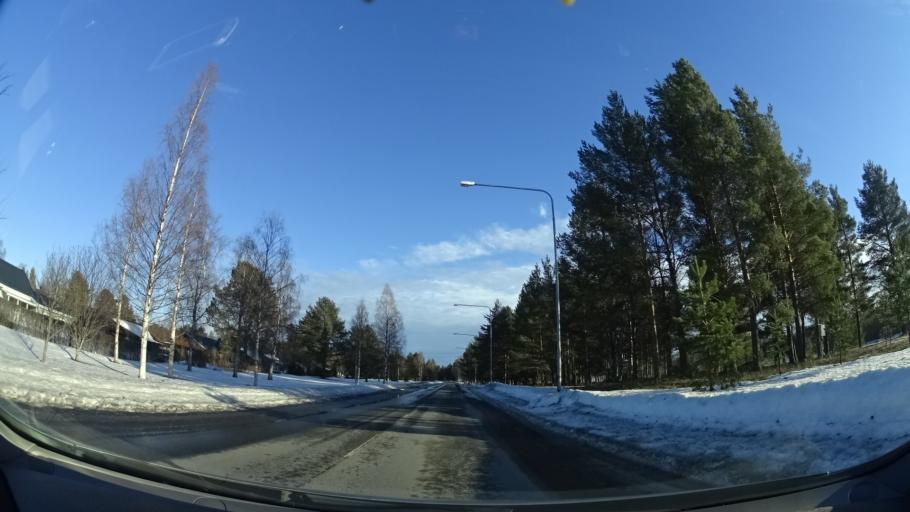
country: SE
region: Vaesterbotten
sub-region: Skelleftea Kommun
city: Byske
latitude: 64.9482
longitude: 21.2248
